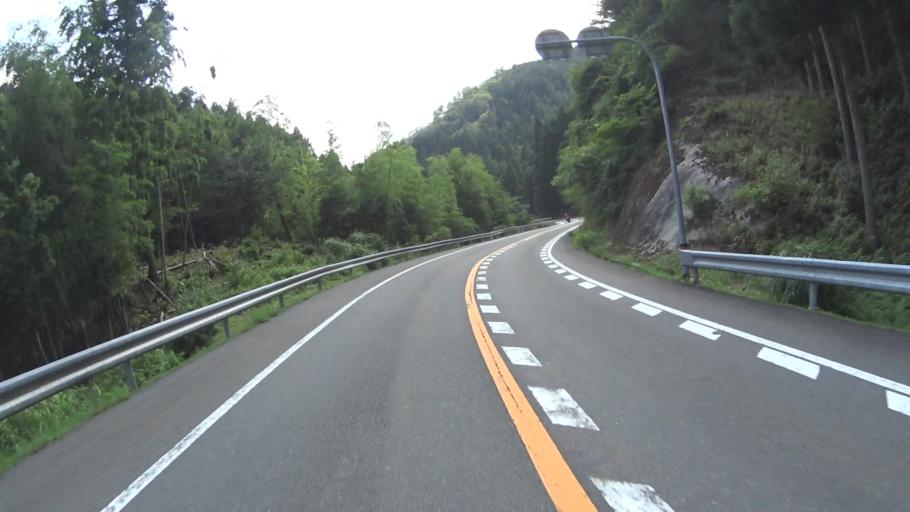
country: JP
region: Fukui
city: Obama
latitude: 35.3584
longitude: 135.5987
